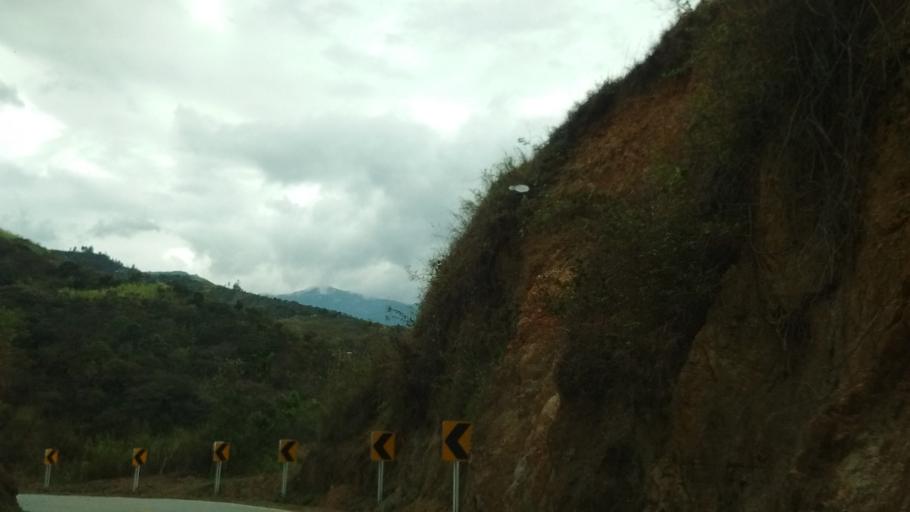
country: CO
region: Cauca
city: La Sierra
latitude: 2.1375
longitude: -76.7712
